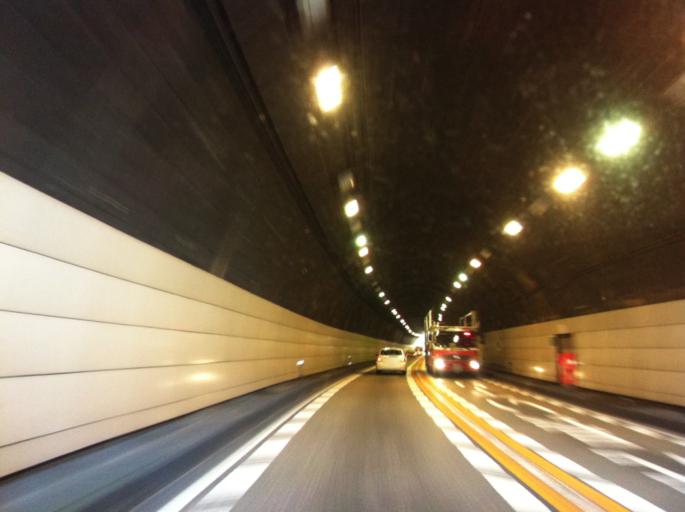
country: JP
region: Shizuoka
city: Kanaya
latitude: 34.8256
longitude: 138.1212
